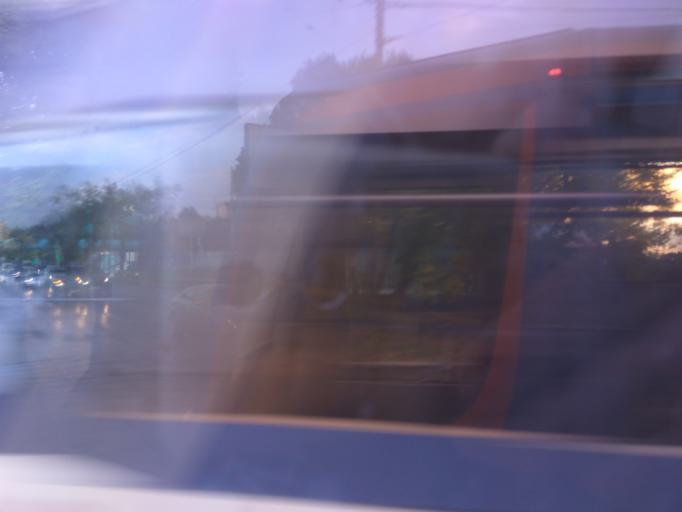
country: RU
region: Moskovskaya
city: Bogorodskoye
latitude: 55.8034
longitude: 37.7079
